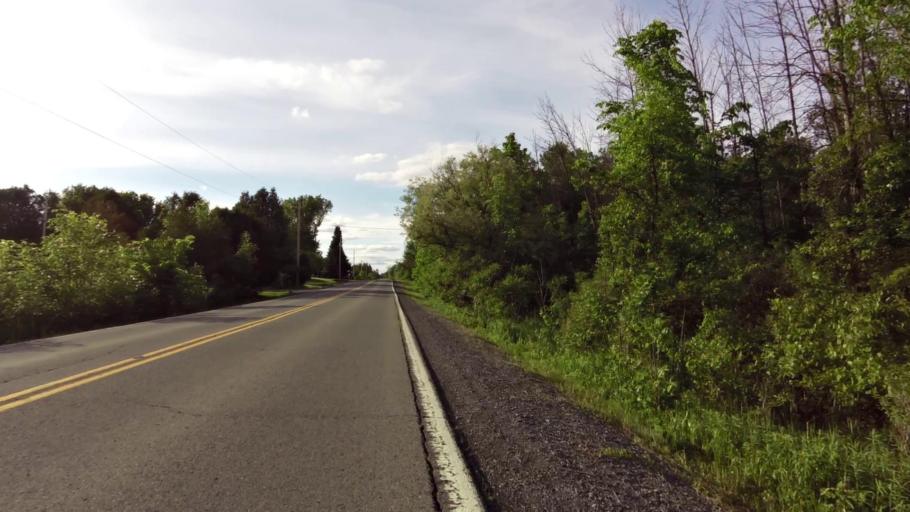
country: CA
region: Ontario
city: Ottawa
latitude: 45.2290
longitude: -75.6079
